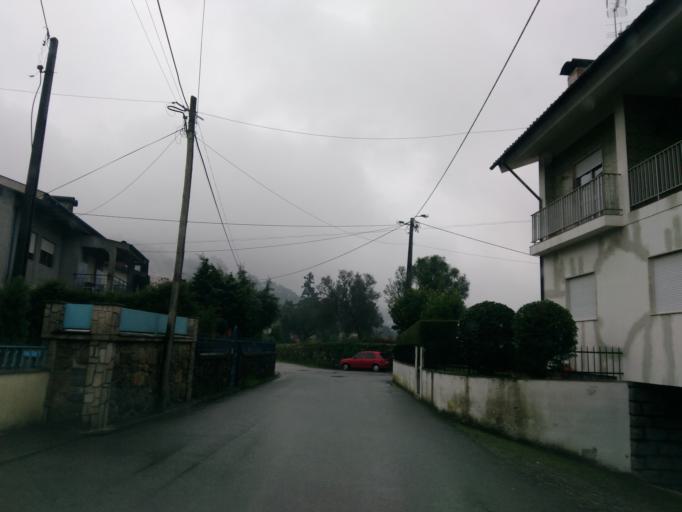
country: PT
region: Braga
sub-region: Braga
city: Adaufe
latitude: 41.5672
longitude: -8.3803
